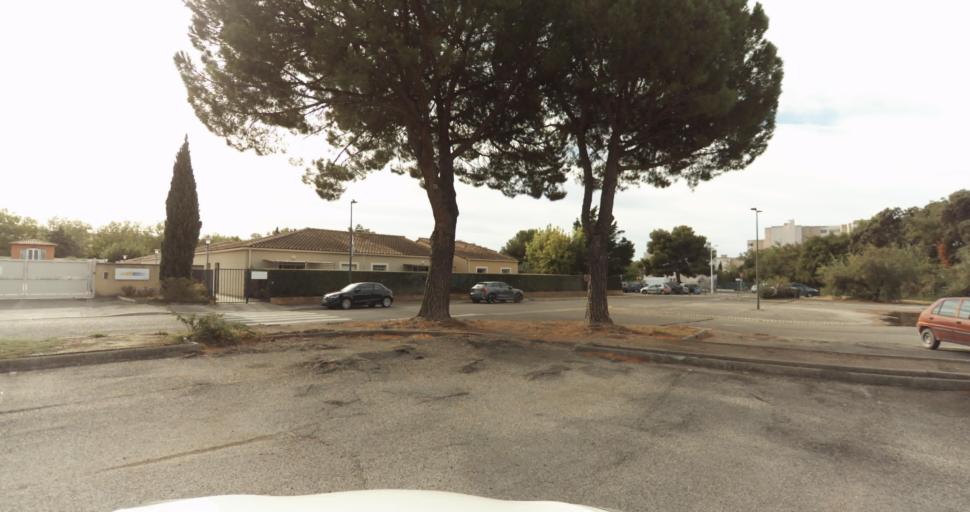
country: FR
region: Provence-Alpes-Cote d'Azur
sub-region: Departement des Bouches-du-Rhone
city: Miramas
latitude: 43.5908
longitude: 5.0018
